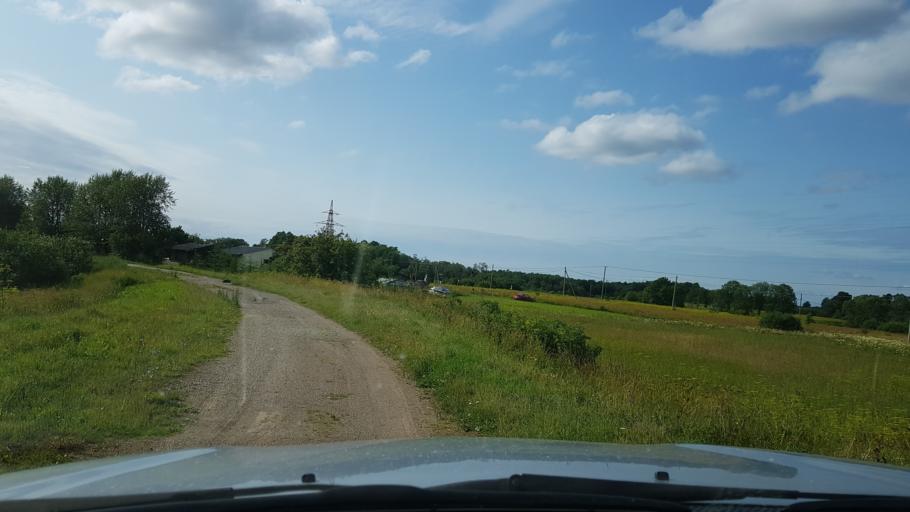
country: EE
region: Ida-Virumaa
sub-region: Narva-Joesuu linn
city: Narva-Joesuu
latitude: 59.4010
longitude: 28.0688
